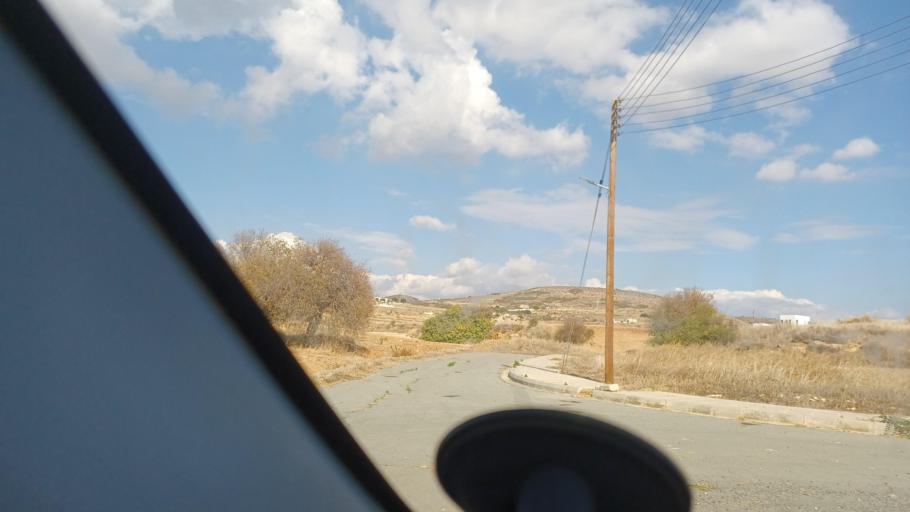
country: CY
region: Pafos
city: Mesogi
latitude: 34.7439
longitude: 32.5311
